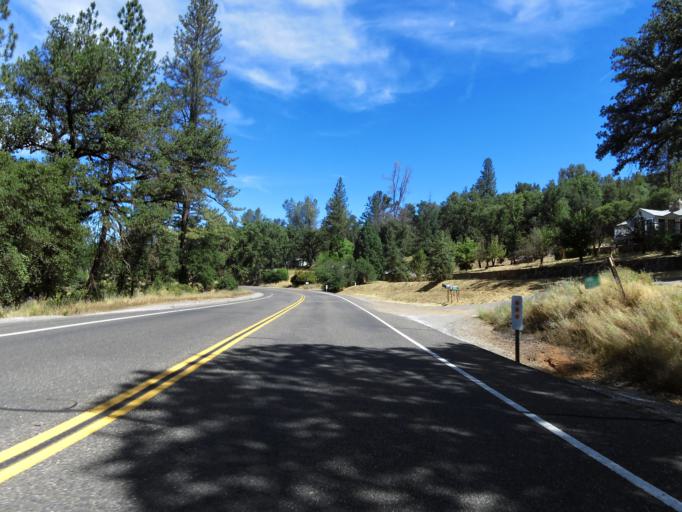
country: US
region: California
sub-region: Mariposa County
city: Midpines
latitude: 37.5582
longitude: -119.9327
